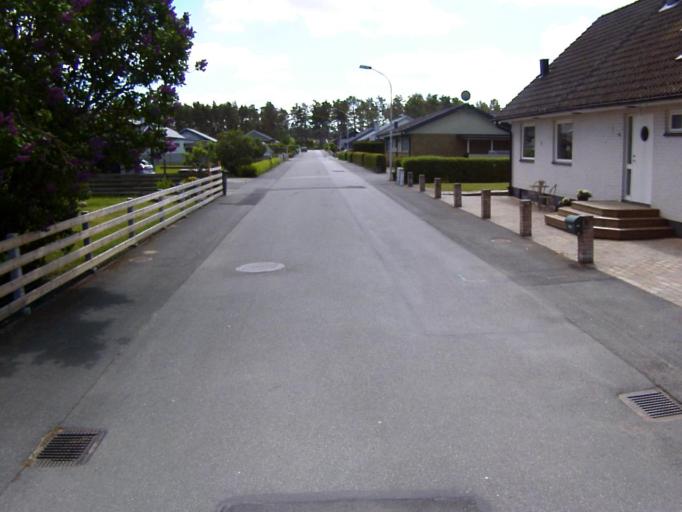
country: SE
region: Skane
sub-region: Kristianstads Kommun
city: Ahus
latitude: 55.9457
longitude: 14.2735
